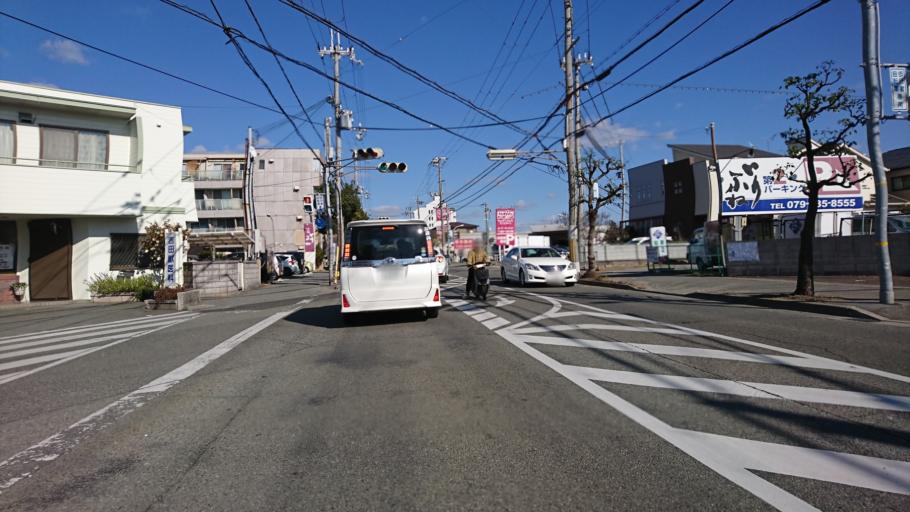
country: JP
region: Hyogo
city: Kakogawacho-honmachi
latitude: 34.7368
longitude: 134.8604
